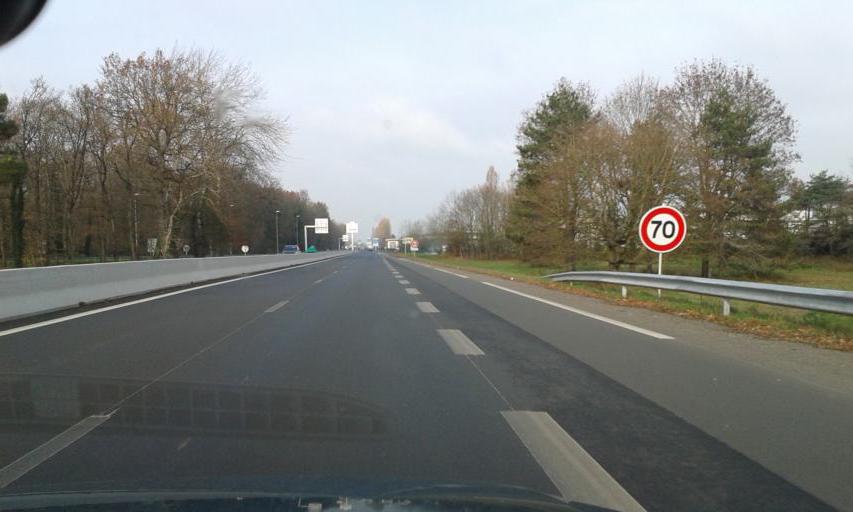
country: FR
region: Centre
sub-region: Departement du Loiret
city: Olivet
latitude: 47.8306
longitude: 1.9192
